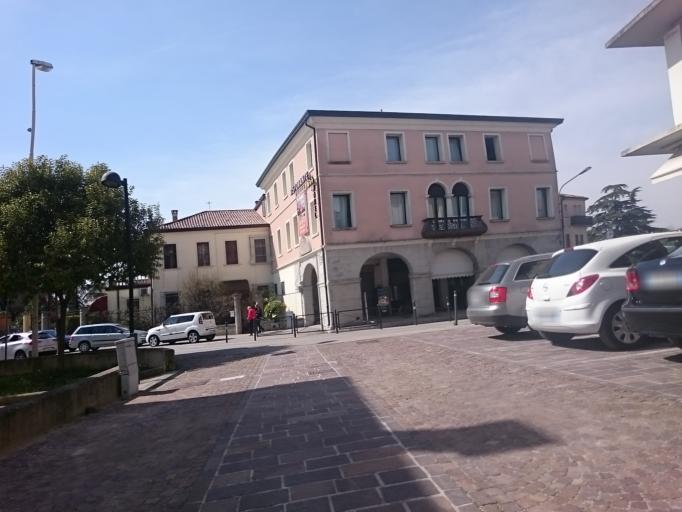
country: IT
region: Veneto
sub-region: Provincia di Padova
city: Limena
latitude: 45.4819
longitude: 11.8435
